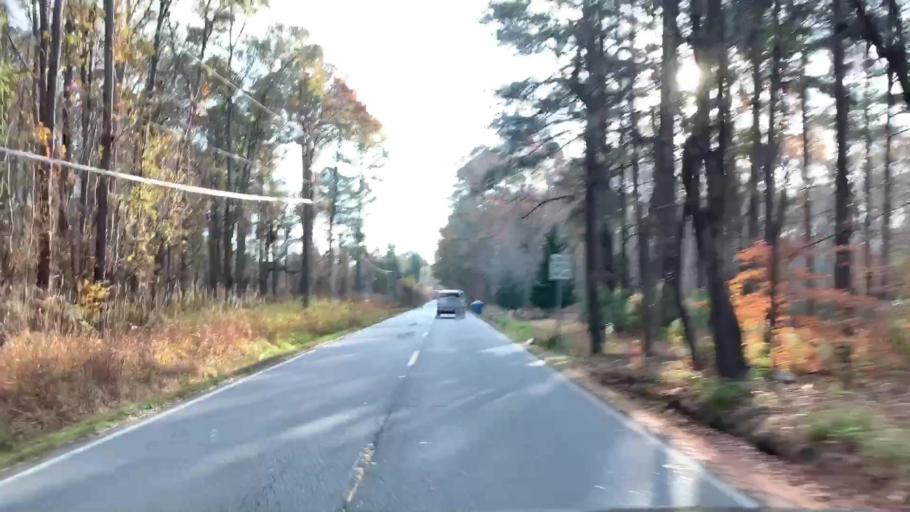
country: US
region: Virginia
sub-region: City of Virginia Beach
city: Virginia Beach
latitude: 36.7386
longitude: -76.1063
